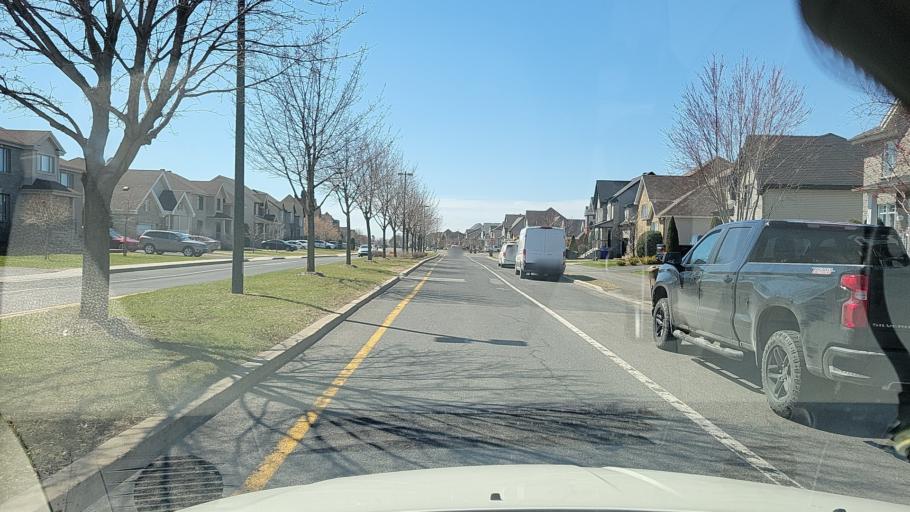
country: CA
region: Quebec
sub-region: Monteregie
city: Sainte-Julie
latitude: 45.5844
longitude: -73.3525
